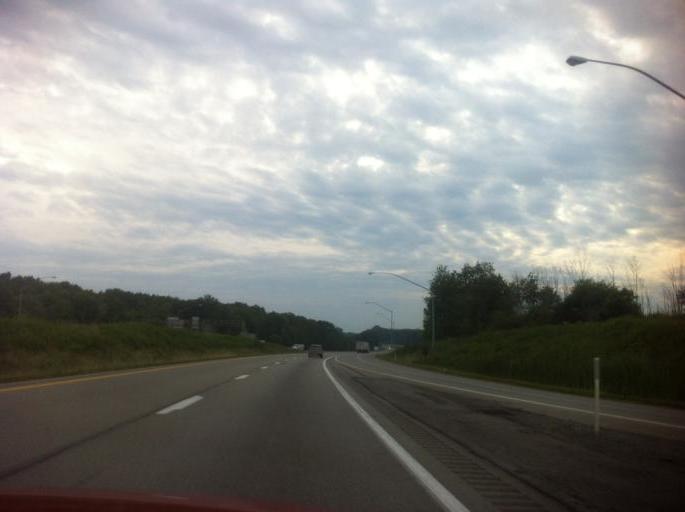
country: US
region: Pennsylvania
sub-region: Mercer County
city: Grove City
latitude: 41.2017
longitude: -79.9777
